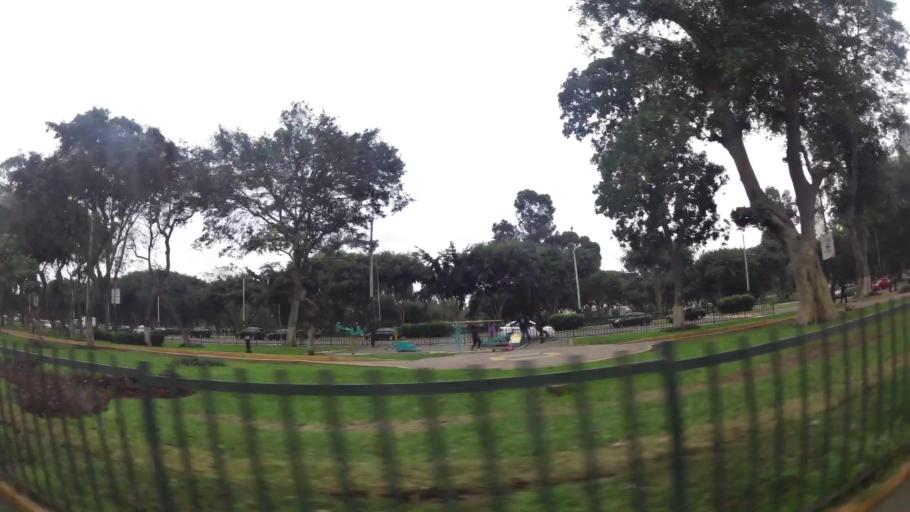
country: PE
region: Lima
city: Lima
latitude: -12.0679
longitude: -77.0441
